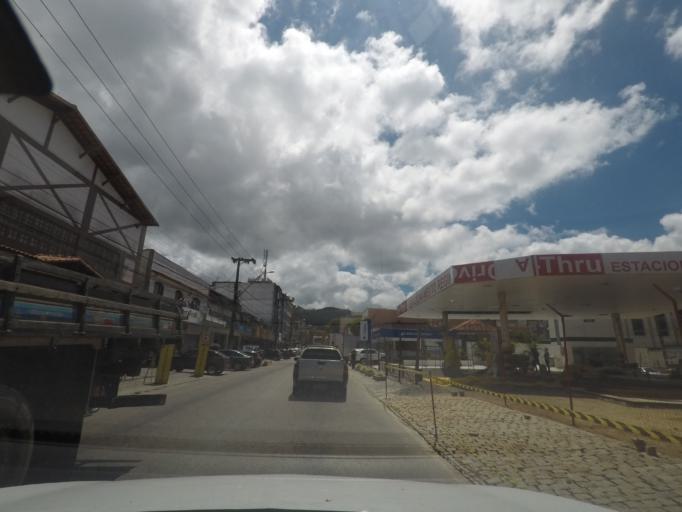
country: BR
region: Rio de Janeiro
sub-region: Teresopolis
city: Teresopolis
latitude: -22.4011
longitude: -42.9788
